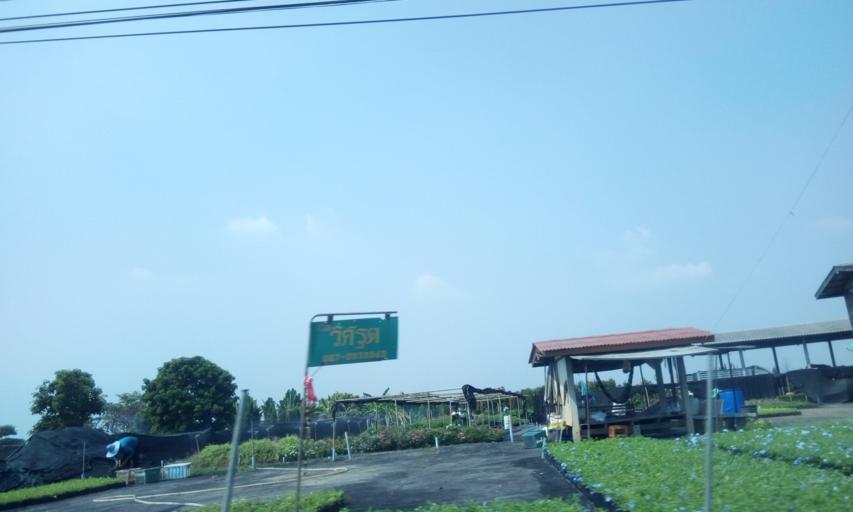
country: TH
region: Nakhon Nayok
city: Ongkharak
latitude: 14.1400
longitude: 100.9710
